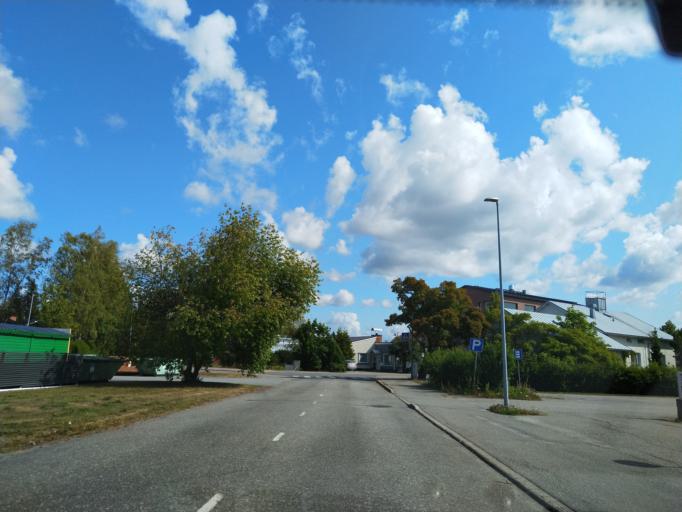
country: FI
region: Satakunta
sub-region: Pori
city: Huittinen
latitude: 61.1780
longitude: 22.6991
